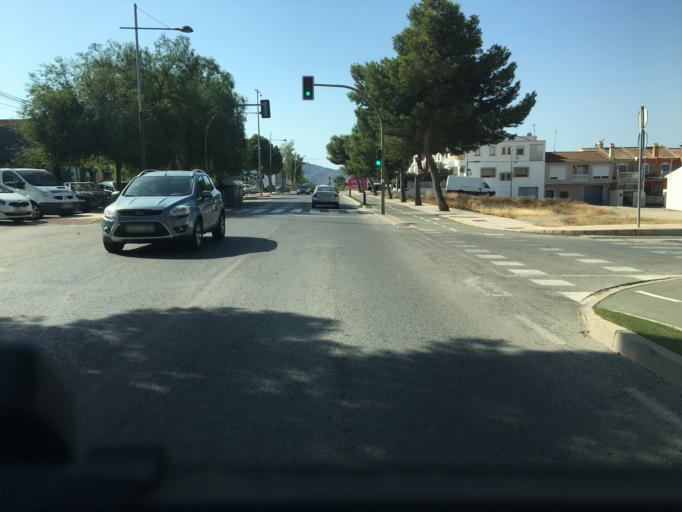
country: ES
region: Andalusia
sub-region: Provincia de Almeria
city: Huercal-Overa
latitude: 37.4028
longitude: -1.9544
